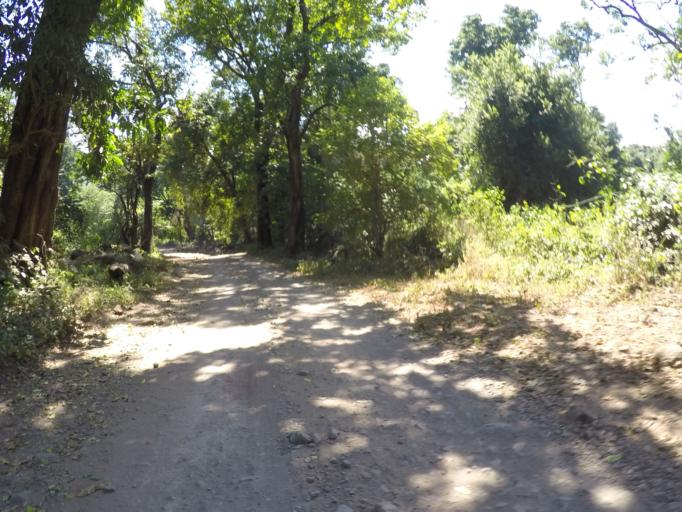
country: TZ
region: Arusha
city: Mto wa Mbu
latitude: -3.4114
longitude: 35.8121
